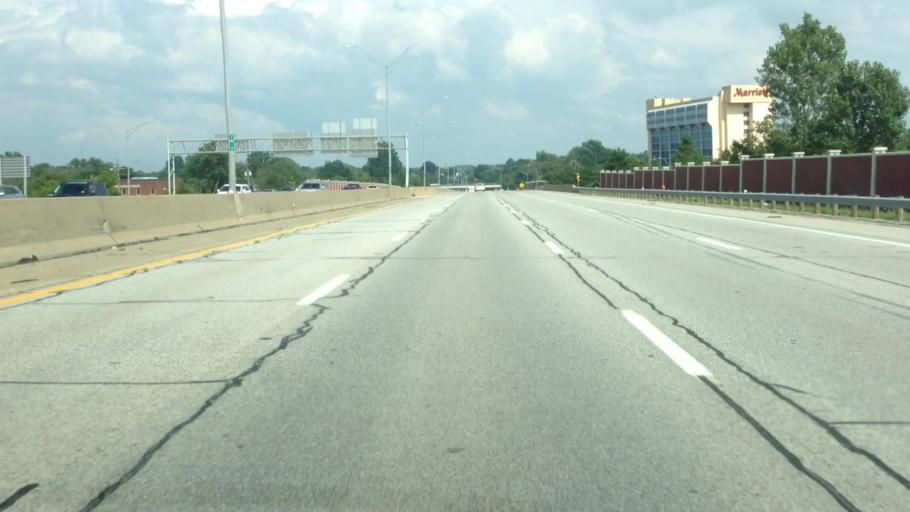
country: US
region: Ohio
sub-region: Cuyahoga County
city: Brook Park
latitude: 41.4388
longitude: -81.8033
